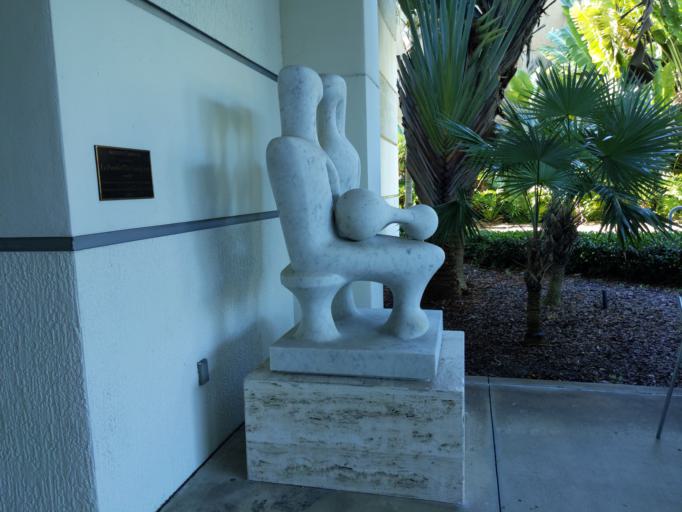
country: US
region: Florida
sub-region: Miami-Dade County
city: Coral Gables
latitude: 25.7228
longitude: -80.2770
